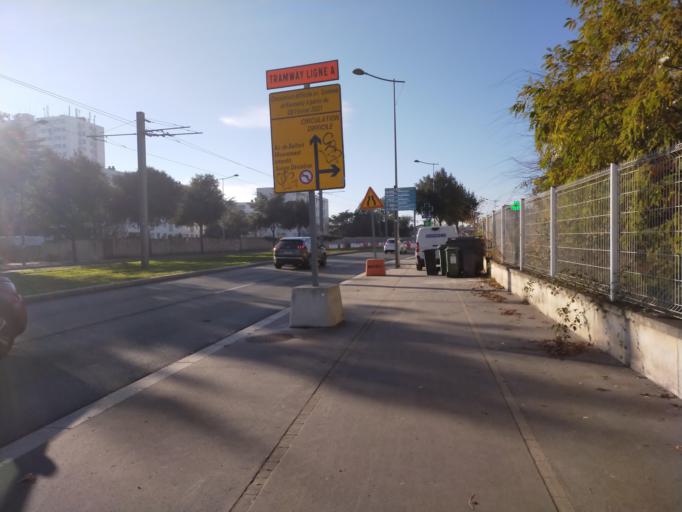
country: FR
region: Aquitaine
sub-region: Departement de la Gironde
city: Merignac
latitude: 44.8324
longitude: -0.6455
